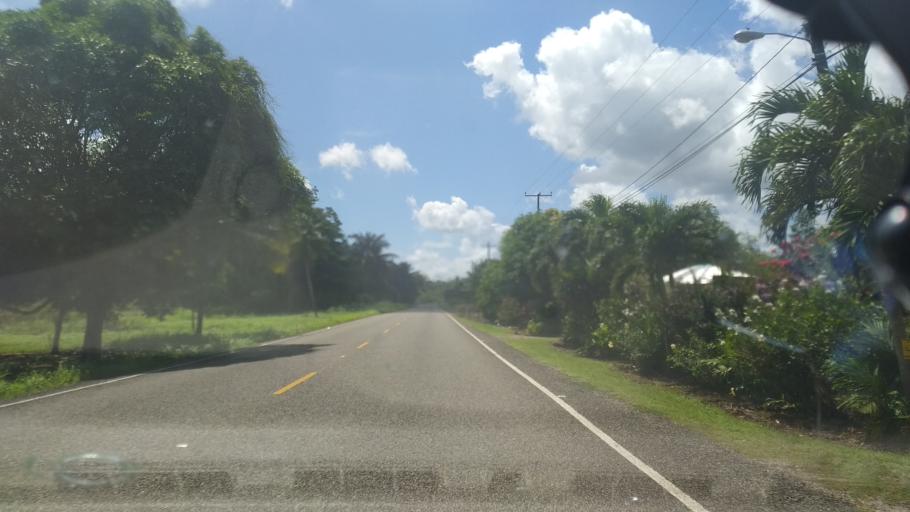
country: BZ
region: Stann Creek
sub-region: Dangriga
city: Dangriga
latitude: 17.0146
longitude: -88.4846
